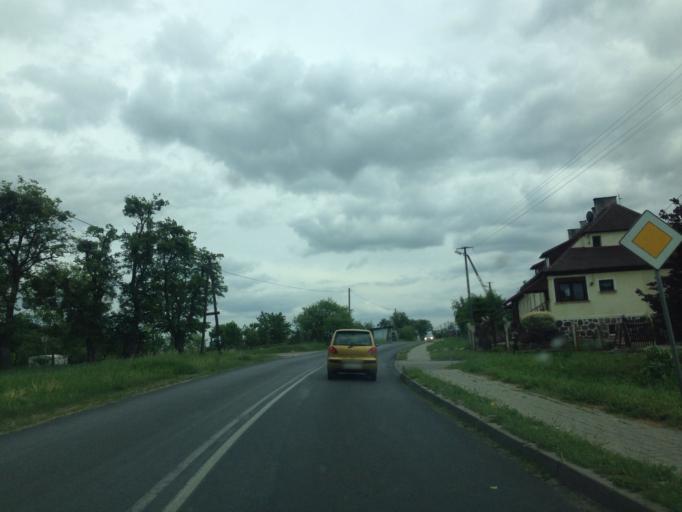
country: PL
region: Kujawsko-Pomorskie
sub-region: Powiat brodnicki
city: Brodnica
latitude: 53.2458
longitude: 19.4625
